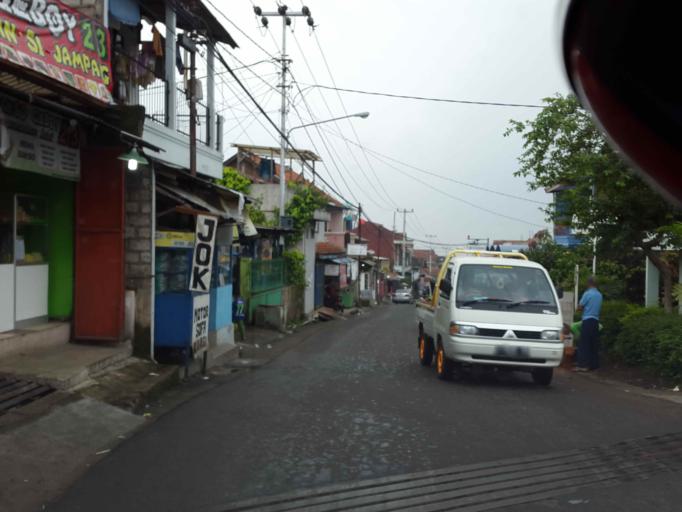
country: ID
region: West Java
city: Cimahi
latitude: -6.8627
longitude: 107.5759
